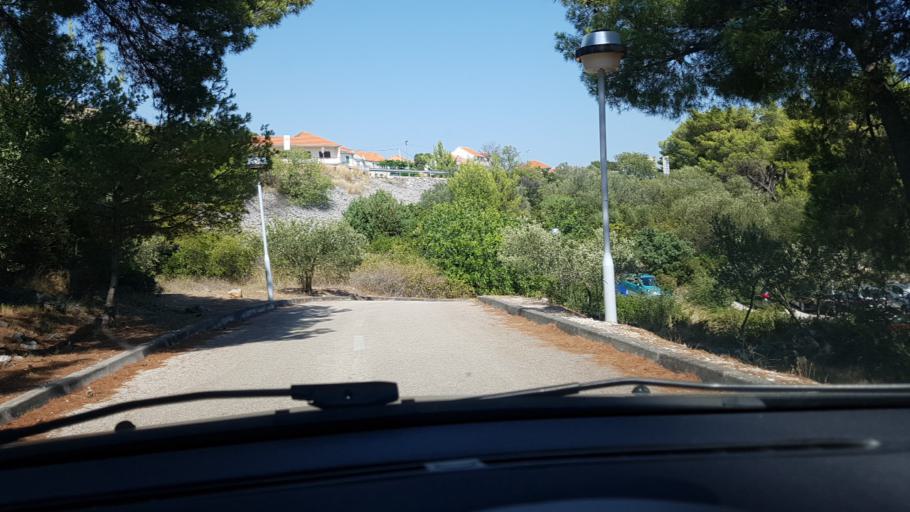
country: HR
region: Splitsko-Dalmatinska
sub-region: Grad Trogir
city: Trogir
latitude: 43.5144
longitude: 16.2082
